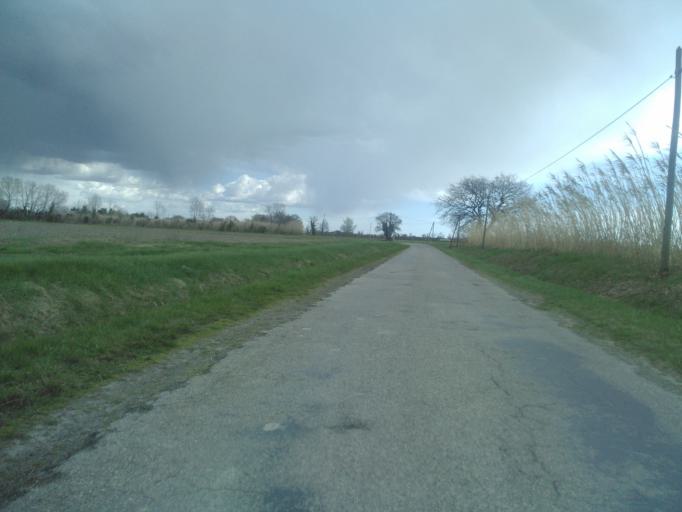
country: FR
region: Provence-Alpes-Cote d'Azur
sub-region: Departement des Bouches-du-Rhone
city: Arles
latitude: 43.6313
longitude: 4.5800
